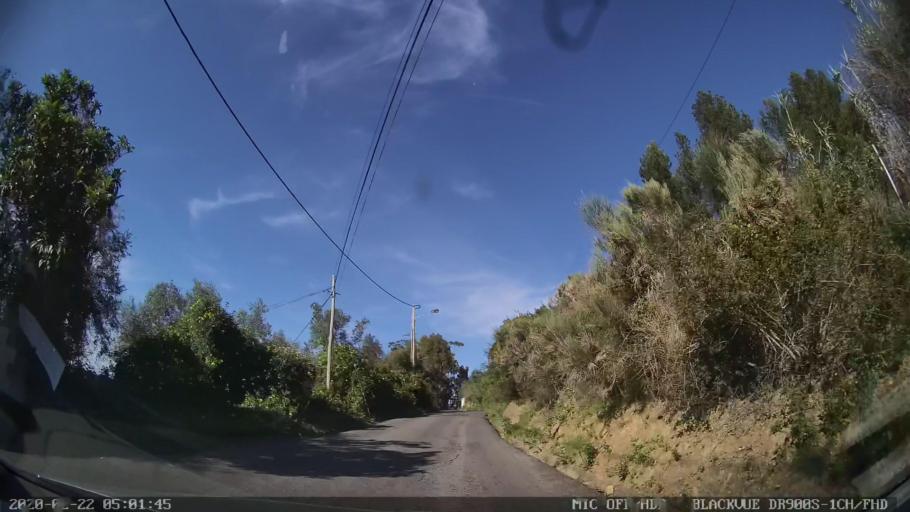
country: PT
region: Lisbon
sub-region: Vila Franca de Xira
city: Vila Franca de Xira
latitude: 38.9613
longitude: -8.9966
